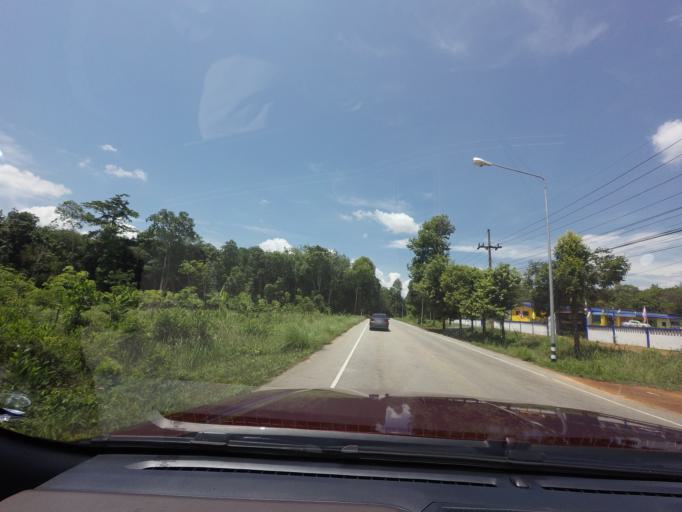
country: TH
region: Narathiwat
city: Chanae
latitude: 6.1867
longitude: 101.6936
